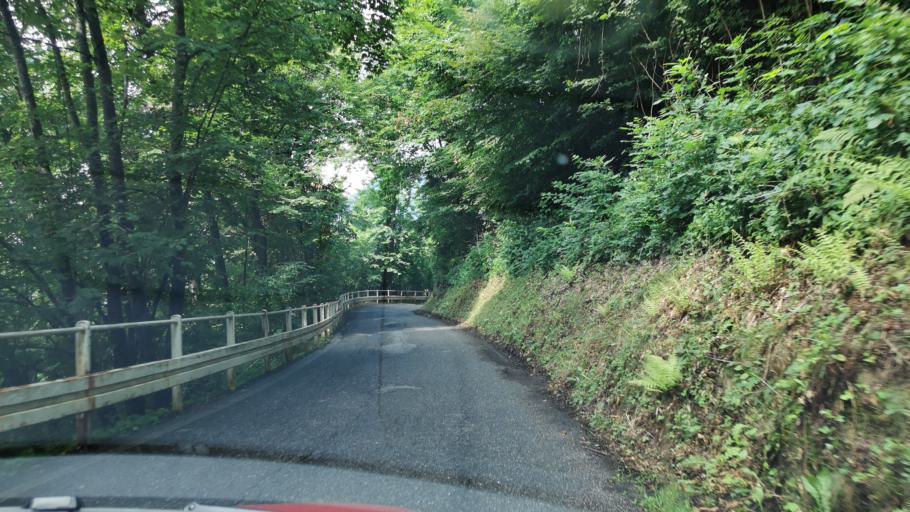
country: IT
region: Lombardy
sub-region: Provincia di Lecco
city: Moggio
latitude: 45.9223
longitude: 9.4888
